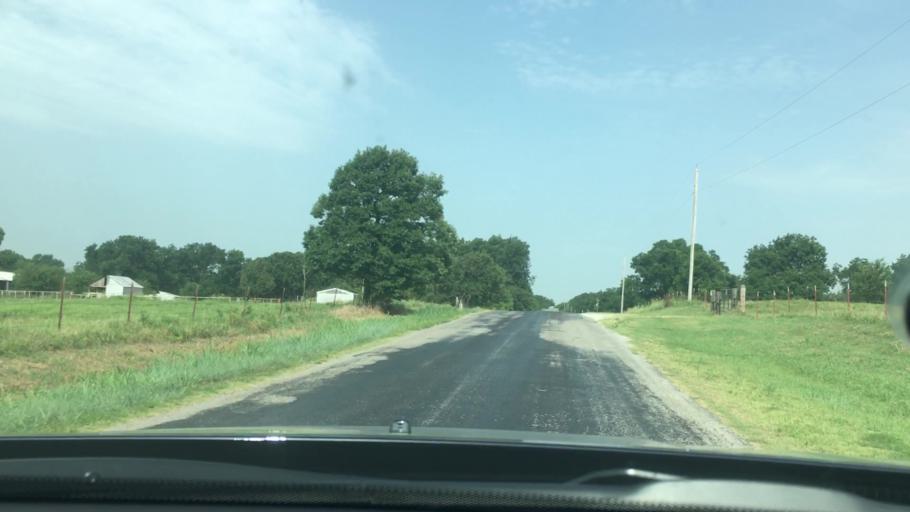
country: US
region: Oklahoma
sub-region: Garvin County
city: Pauls Valley
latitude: 34.8258
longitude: -97.2035
